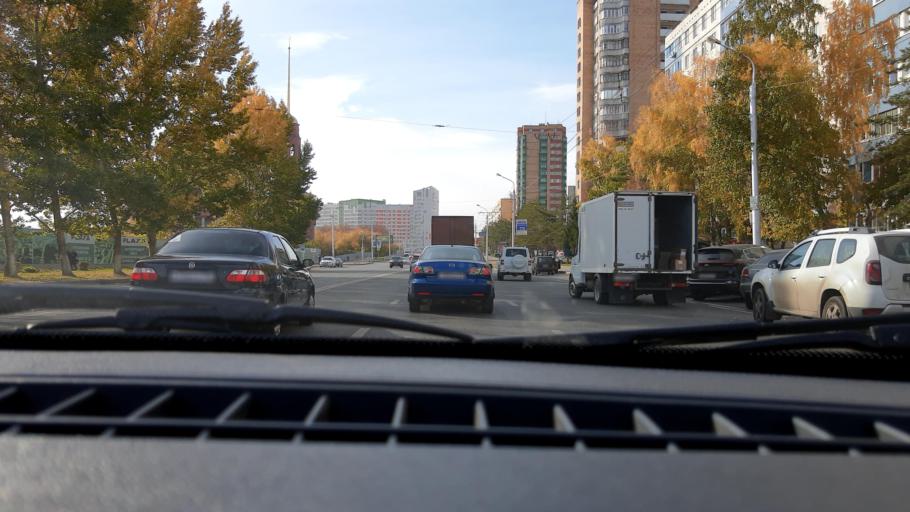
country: RU
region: Bashkortostan
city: Ufa
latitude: 54.7661
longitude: 56.0271
